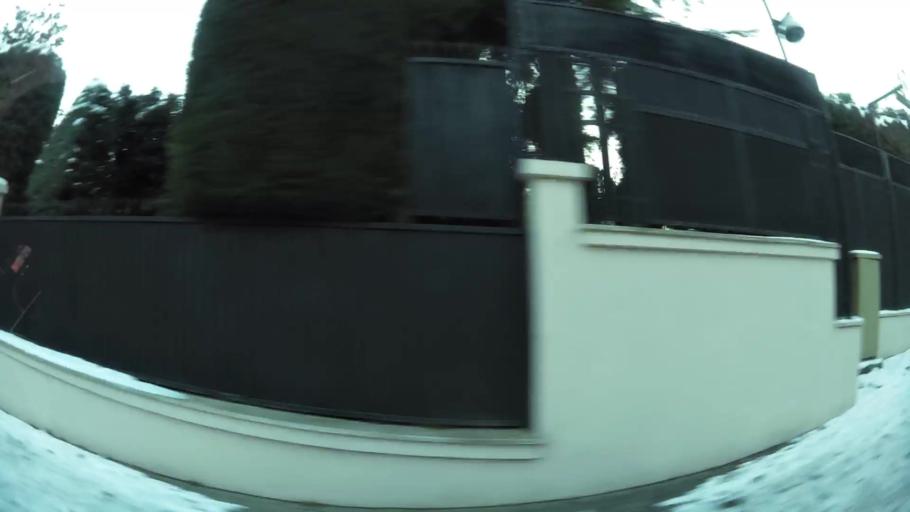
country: MK
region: Karpos
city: Skopje
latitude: 41.9880
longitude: 21.4150
